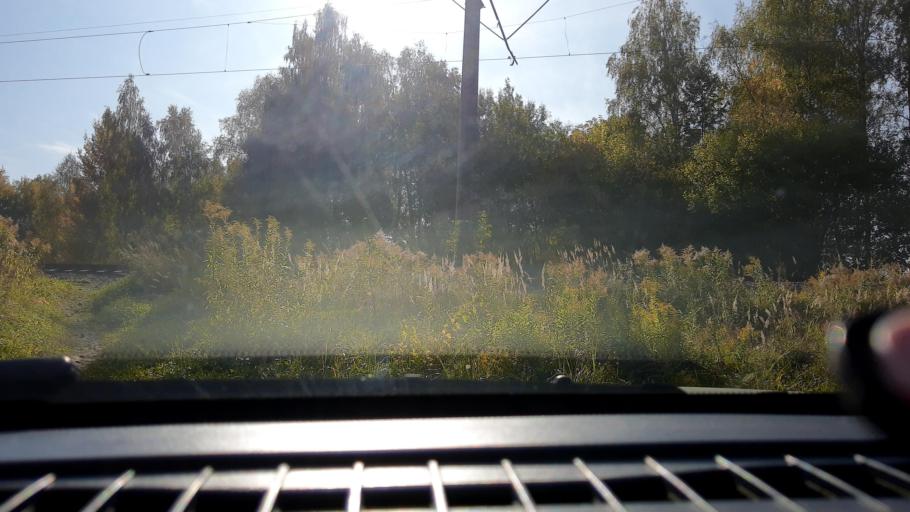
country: RU
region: Nizjnij Novgorod
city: Afonino
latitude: 56.2339
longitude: 44.0639
